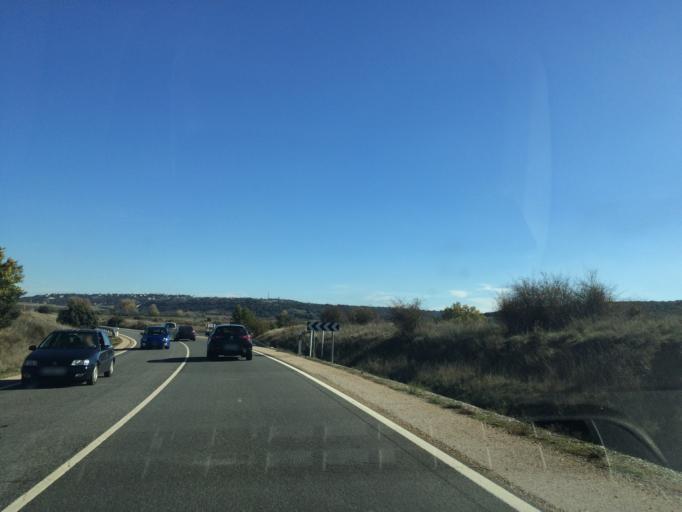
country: ES
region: Madrid
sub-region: Provincia de Madrid
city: Venturada
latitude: 40.7806
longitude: -3.6427
